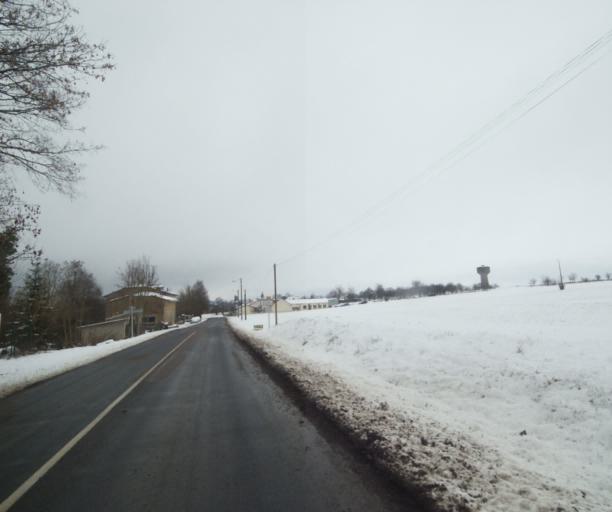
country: FR
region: Champagne-Ardenne
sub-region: Departement de la Haute-Marne
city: Wassy
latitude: 48.4347
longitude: 4.9613
